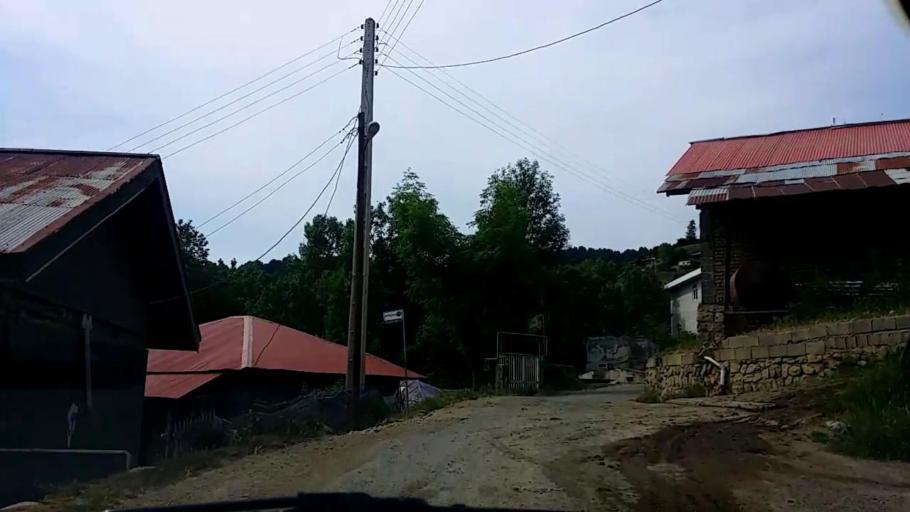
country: IR
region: Mazandaran
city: `Abbasabad
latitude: 36.5540
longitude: 51.1810
